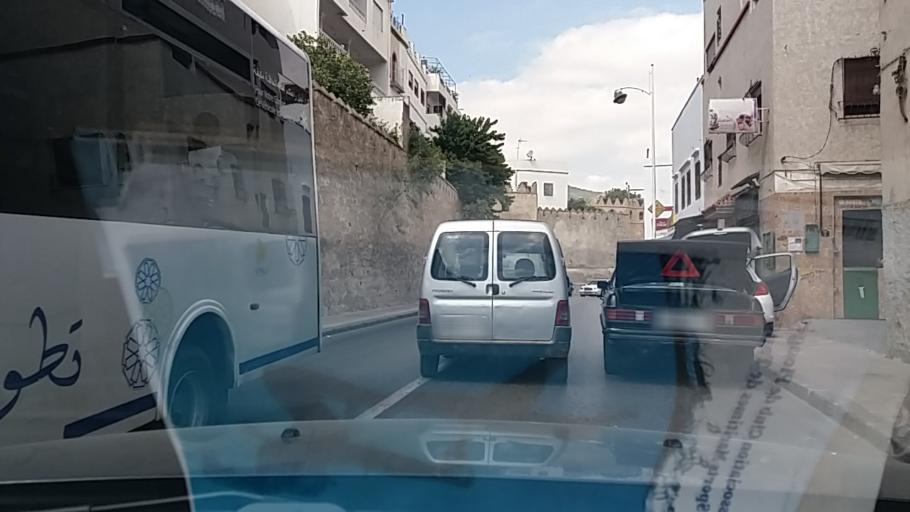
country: MA
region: Tanger-Tetouan
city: Tetouan
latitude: 35.5736
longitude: -5.3636
